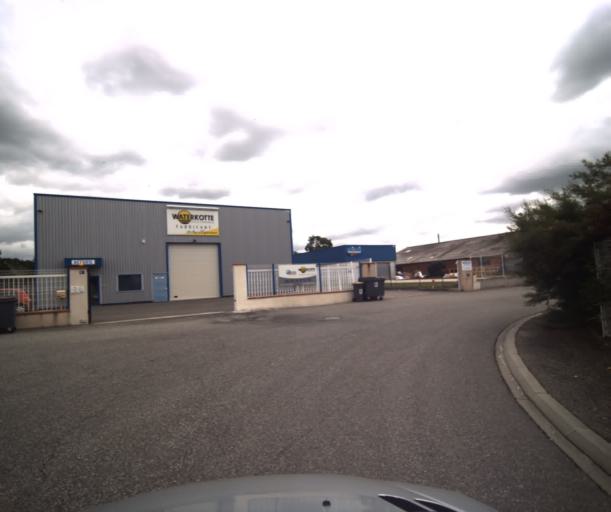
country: FR
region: Midi-Pyrenees
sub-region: Departement de la Haute-Garonne
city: Lacroix-Falgarde
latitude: 43.4909
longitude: 1.3964
